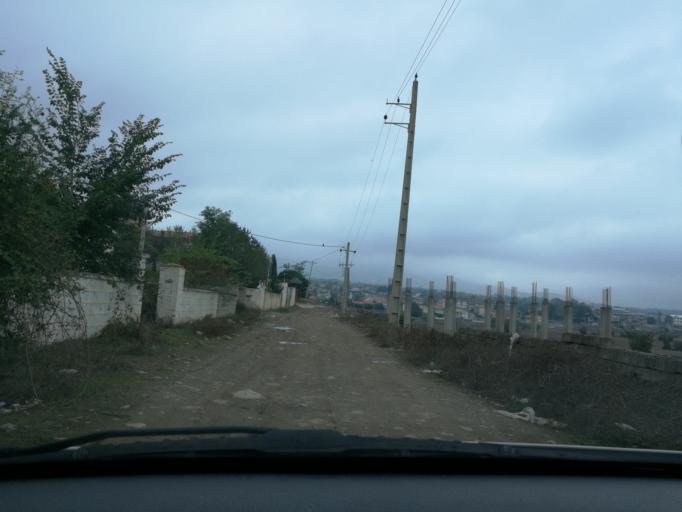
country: IR
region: Mazandaran
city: `Abbasabad
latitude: 36.5024
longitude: 51.2068
